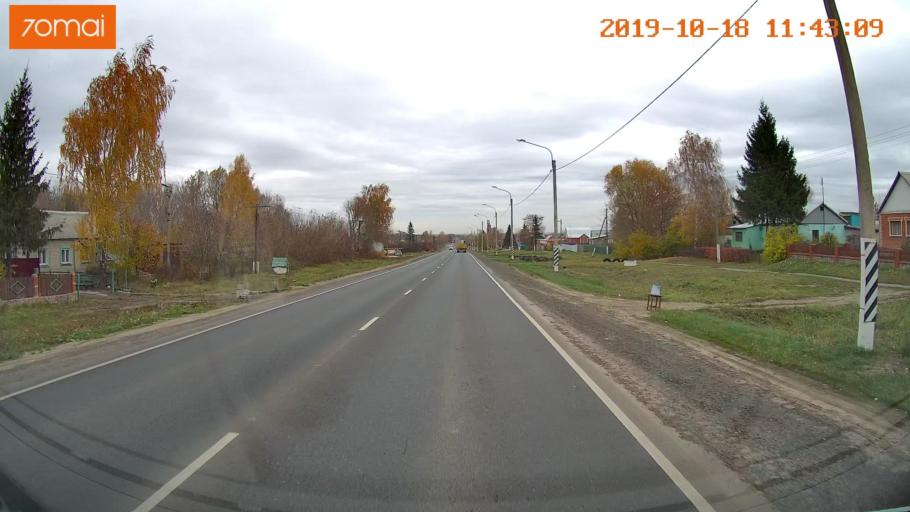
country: RU
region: Rjazan
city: Oktyabr'skiy
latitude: 54.1943
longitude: 38.9393
